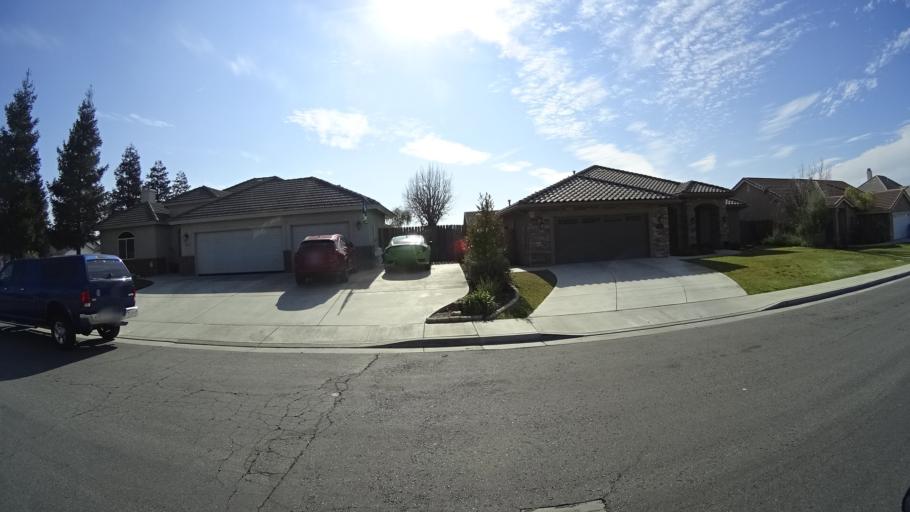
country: US
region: California
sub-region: Kern County
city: Lamont
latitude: 35.3891
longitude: -118.8836
